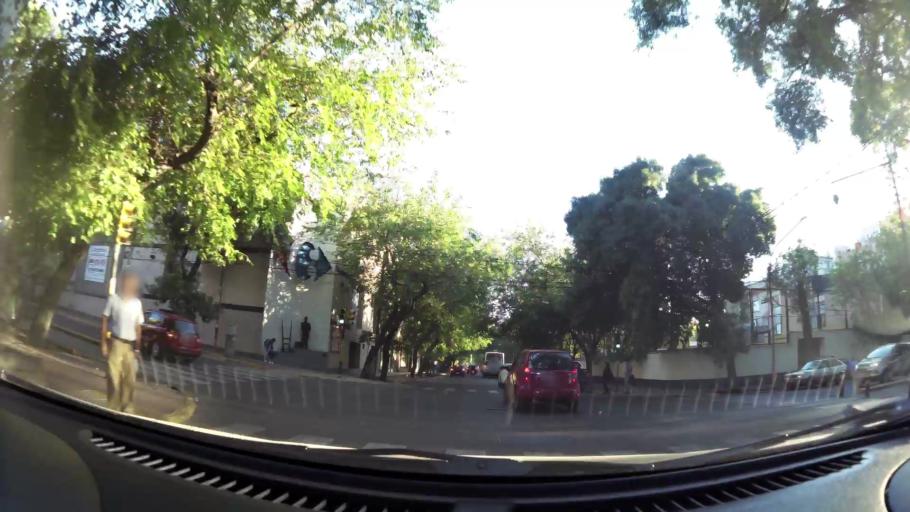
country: AR
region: Mendoza
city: Mendoza
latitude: -32.8858
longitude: -68.8475
